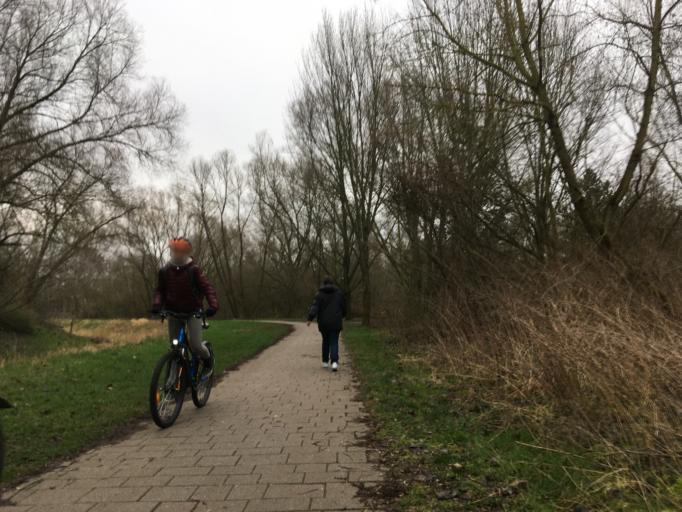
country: DE
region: Berlin
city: Stadtrandsiedlung Malchow
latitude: 52.5718
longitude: 13.4868
